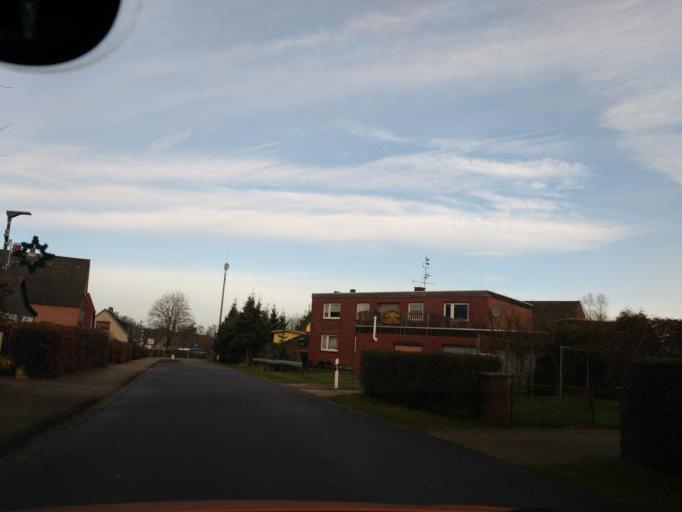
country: DE
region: Lower Saxony
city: Hude
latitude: 53.1093
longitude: 8.4578
